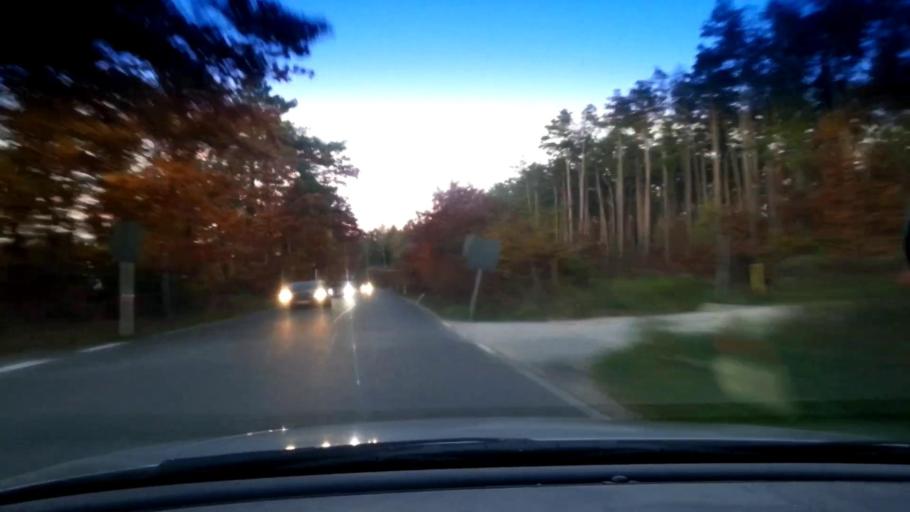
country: DE
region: Bavaria
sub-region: Upper Franconia
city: Bamberg
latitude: 49.8951
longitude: 10.9304
